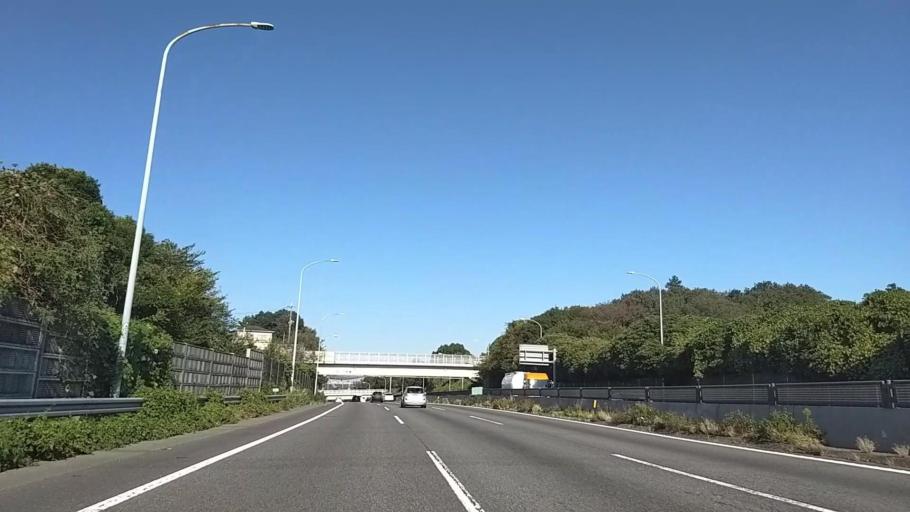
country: JP
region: Kanagawa
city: Minami-rinkan
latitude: 35.4720
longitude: 139.5316
